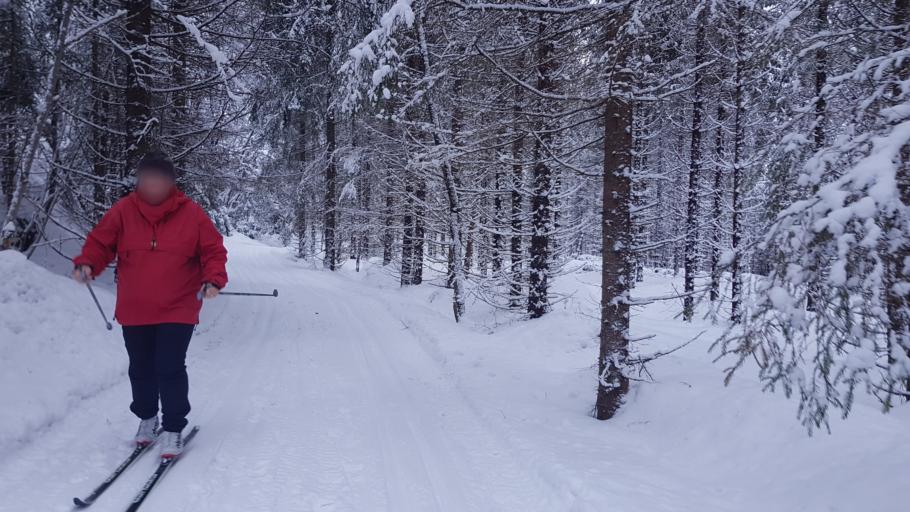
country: NO
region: Akershus
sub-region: Lorenskog
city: Kjenn
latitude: 59.9009
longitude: 10.8769
